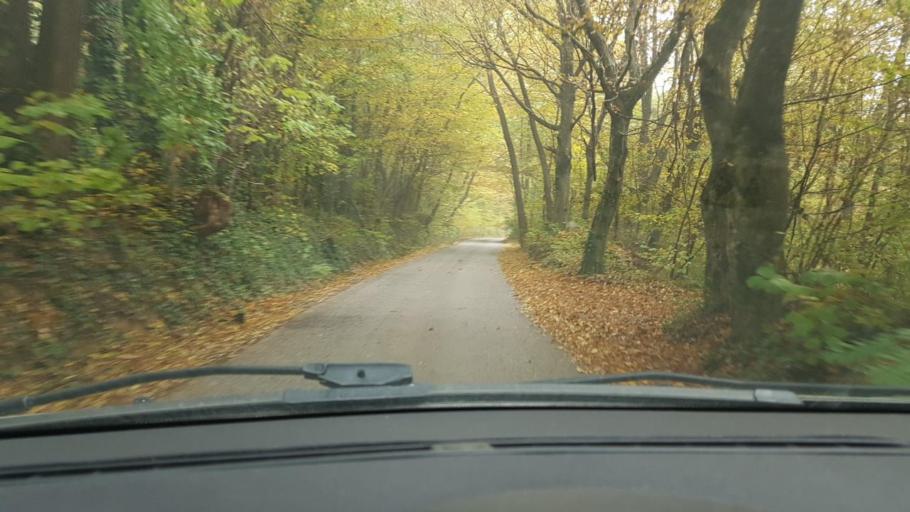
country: HR
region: Krapinsko-Zagorska
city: Zlatar
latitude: 46.1346
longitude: 16.0809
